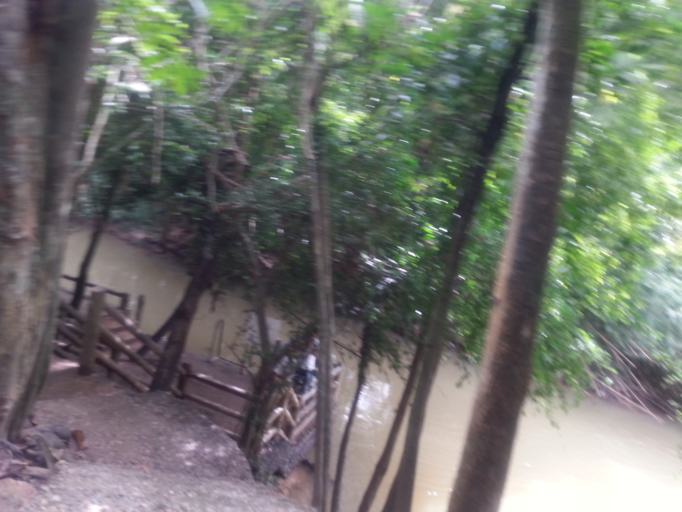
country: TH
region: Krabi
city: Khlong Thom
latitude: 7.9314
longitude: 99.2048
